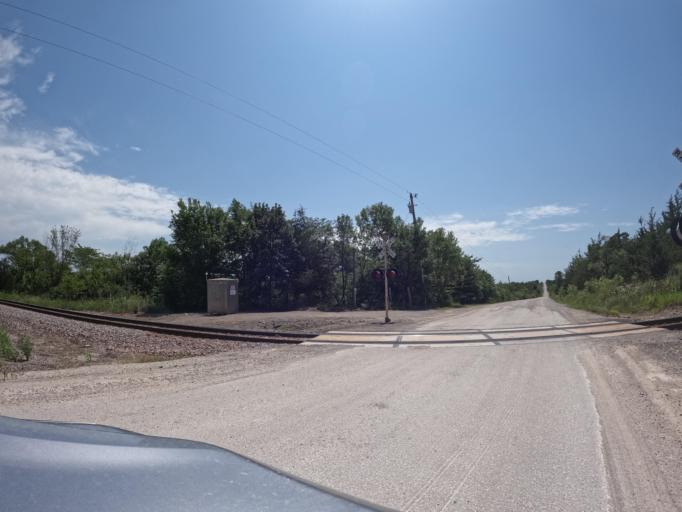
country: US
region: Iowa
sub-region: Appanoose County
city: Centerville
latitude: 40.7824
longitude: -92.9064
